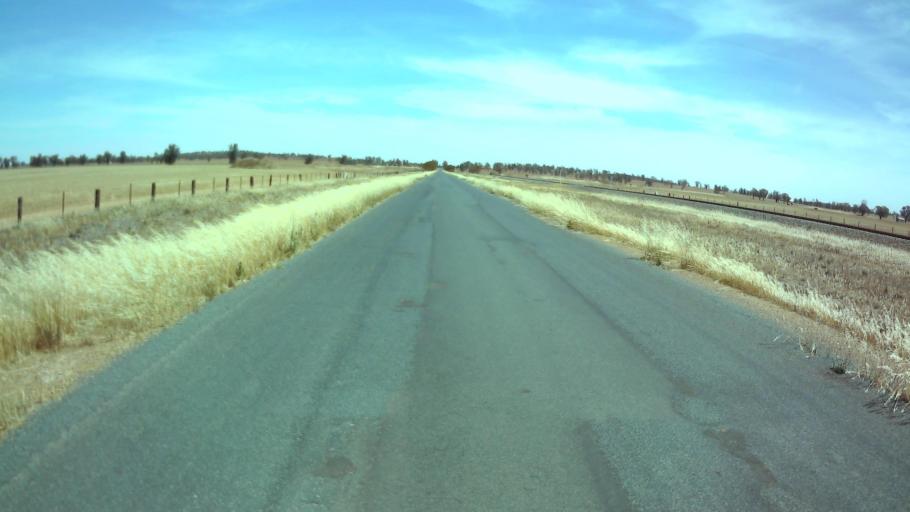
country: AU
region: New South Wales
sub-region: Weddin
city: Grenfell
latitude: -33.7564
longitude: 147.7628
